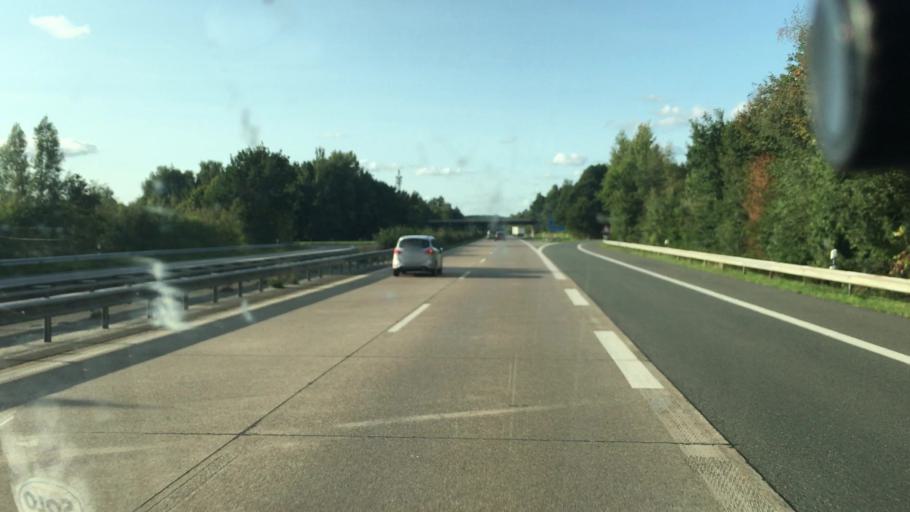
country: DE
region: Lower Saxony
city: Wiefelstede
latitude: 53.2776
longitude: 8.1570
